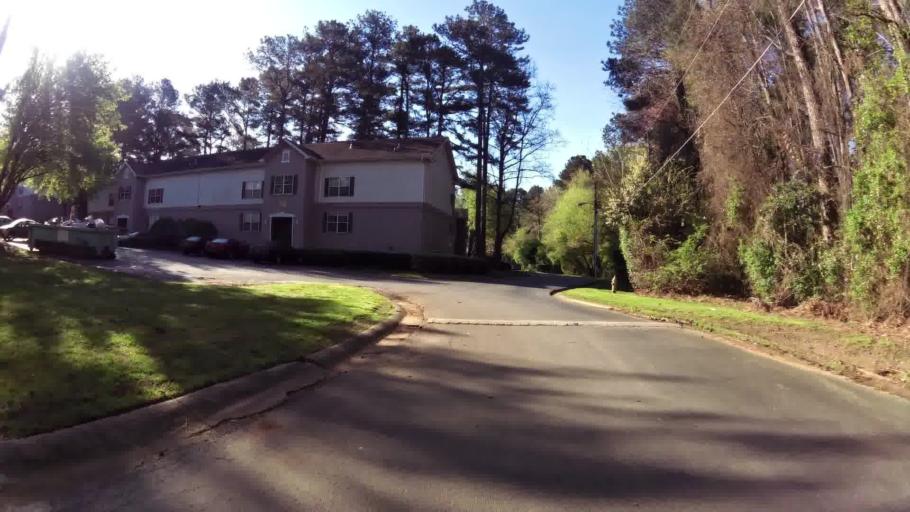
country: US
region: Georgia
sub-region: DeKalb County
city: Clarkston
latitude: 33.8378
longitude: -84.2623
